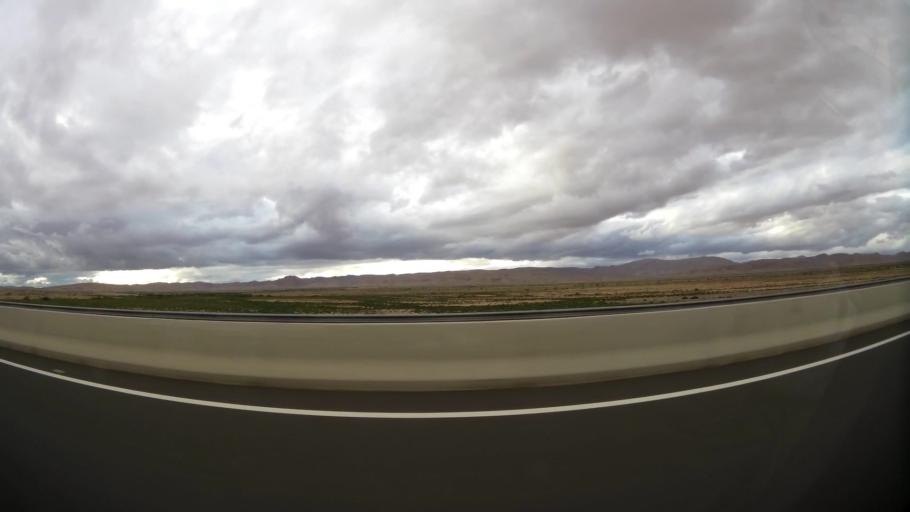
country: MA
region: Taza-Al Hoceima-Taounate
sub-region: Taza
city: Guercif
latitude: 34.3068
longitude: -3.6175
